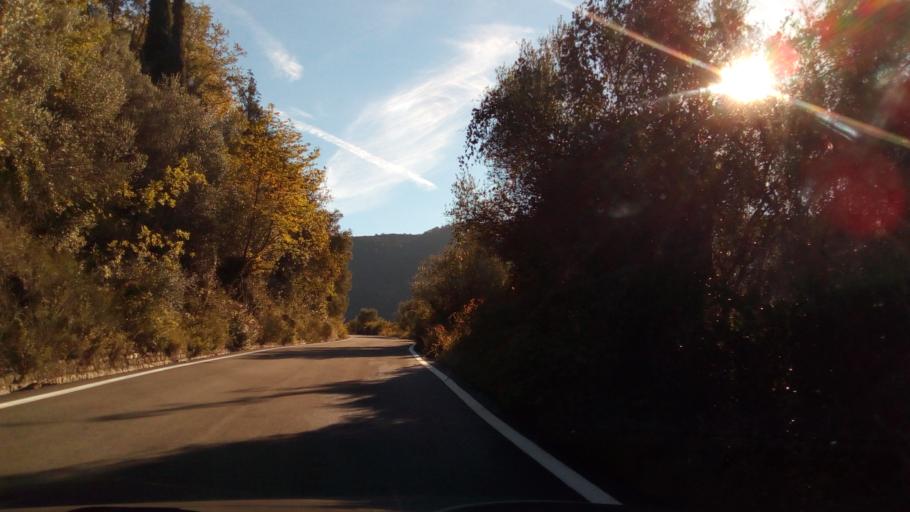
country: GR
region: West Greece
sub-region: Nomos Aitolias kai Akarnanias
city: Nafpaktos
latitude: 38.4673
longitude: 21.8793
